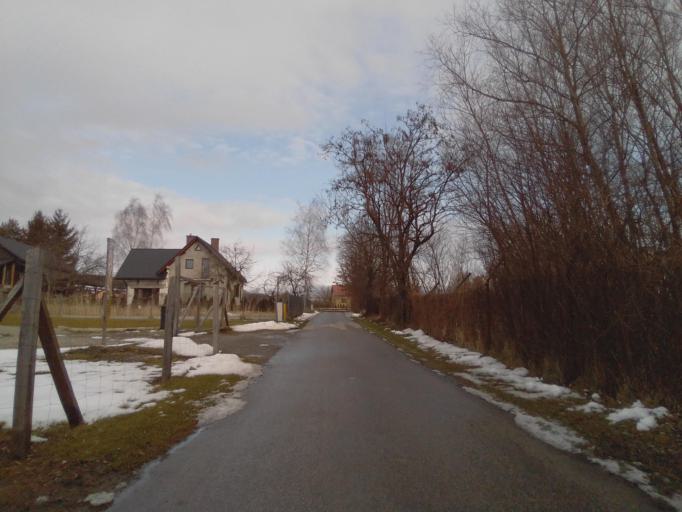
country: PL
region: Subcarpathian Voivodeship
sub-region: Powiat przemyski
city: Nienadowa
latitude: 49.8168
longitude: 22.4156
